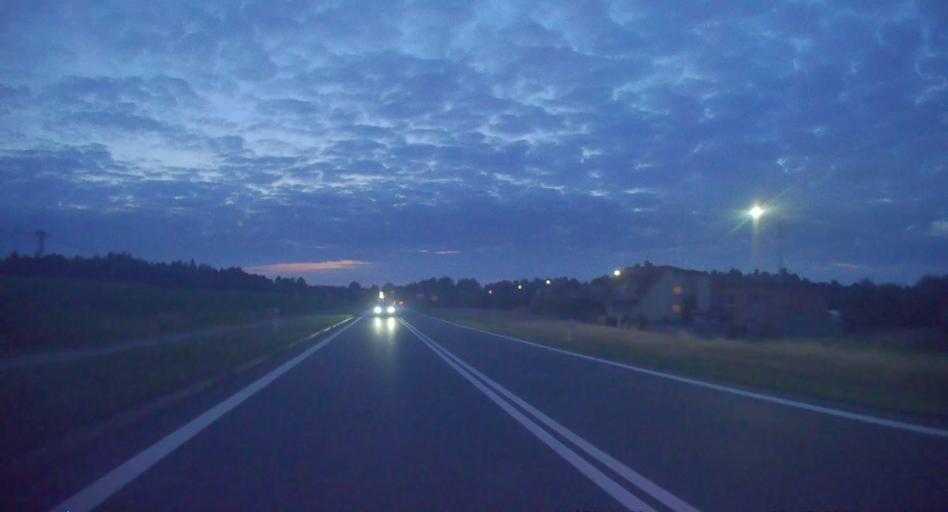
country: PL
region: Silesian Voivodeship
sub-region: Powiat klobucki
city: Kamyk
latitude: 50.8642
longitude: 19.0188
